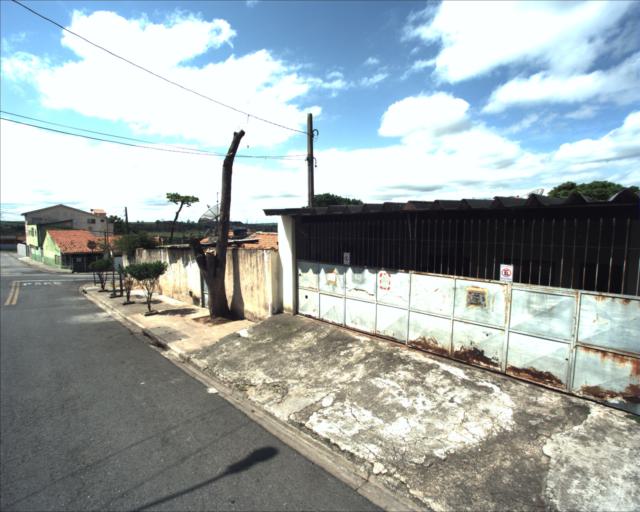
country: BR
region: Sao Paulo
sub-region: Sorocaba
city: Sorocaba
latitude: -23.3953
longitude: -47.3765
